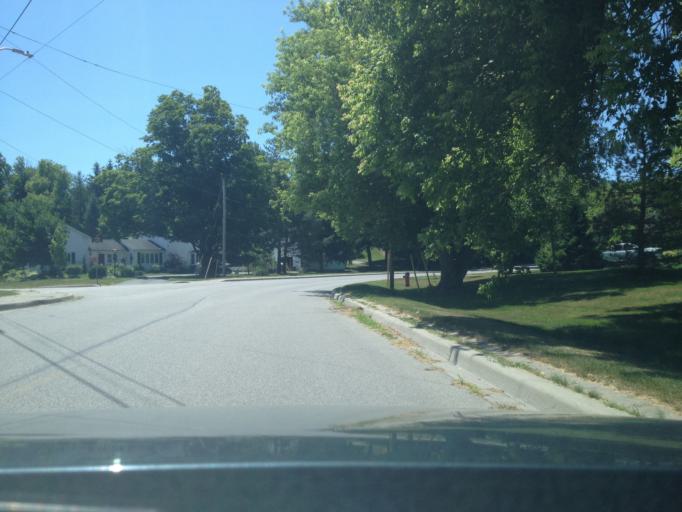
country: CA
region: Ontario
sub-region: Halton
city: Milton
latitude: 43.6662
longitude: -79.9274
